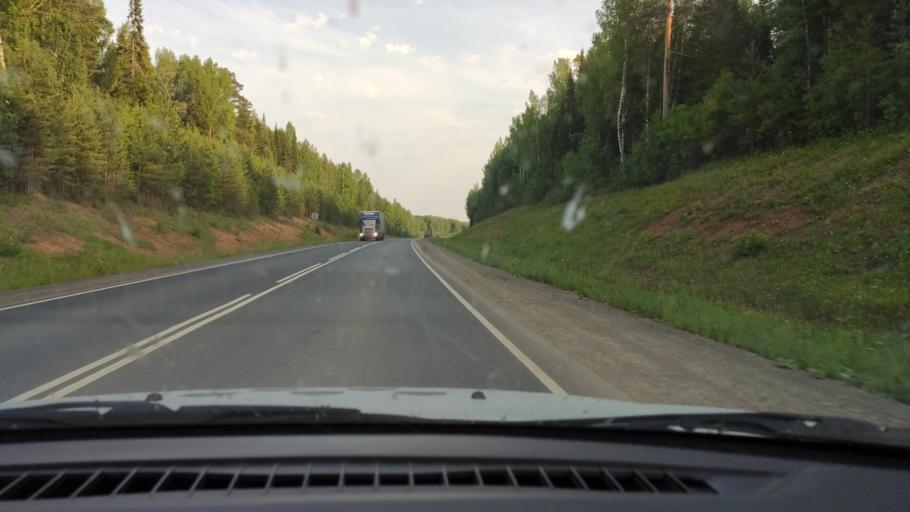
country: RU
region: Perm
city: Siva
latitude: 58.4457
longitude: 54.4274
